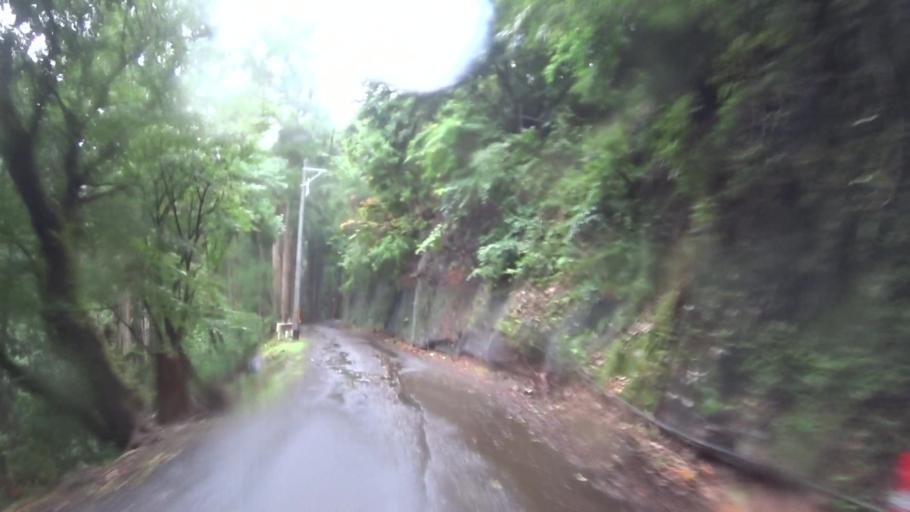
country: JP
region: Shiga Prefecture
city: Kitahama
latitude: 35.2680
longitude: 135.7992
